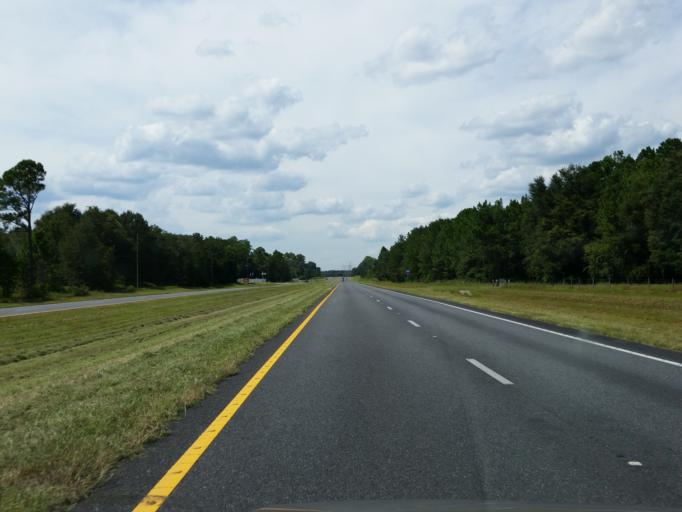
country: US
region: Florida
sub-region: Sumter County
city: Wildwood
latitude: 28.8577
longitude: -82.0718
